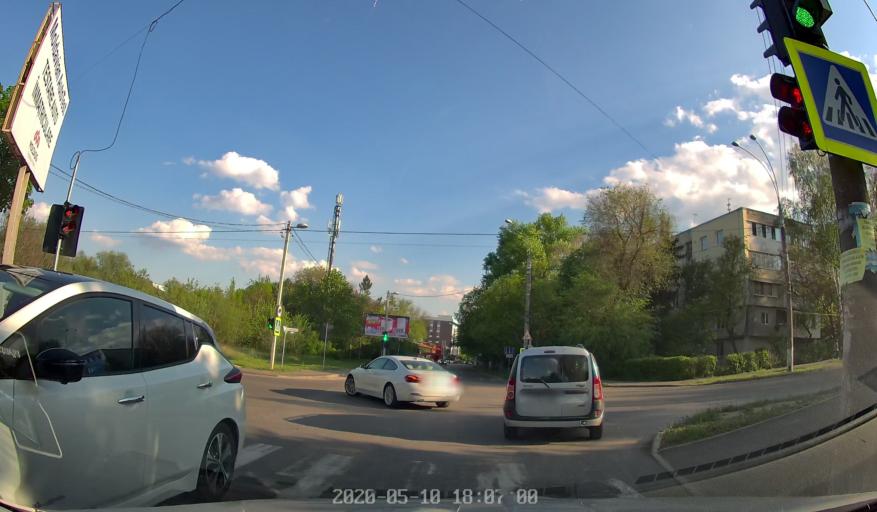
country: MD
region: Chisinau
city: Stauceni
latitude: 47.0601
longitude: 28.8734
